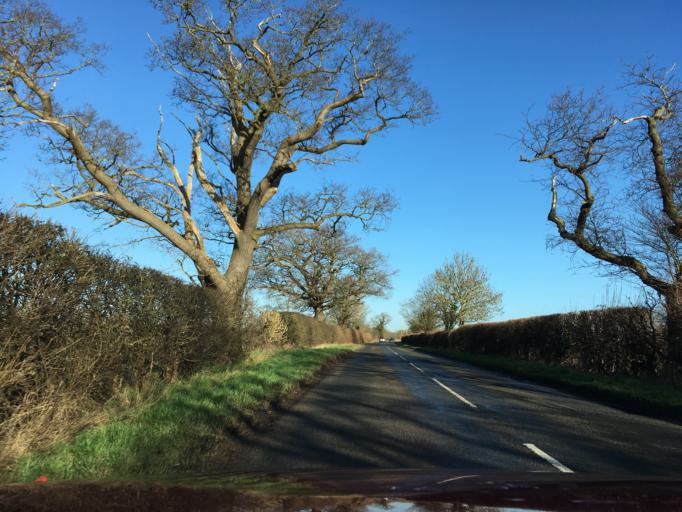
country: GB
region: England
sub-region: Warwickshire
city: Wellesbourne Mountford
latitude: 52.2136
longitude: -1.6095
